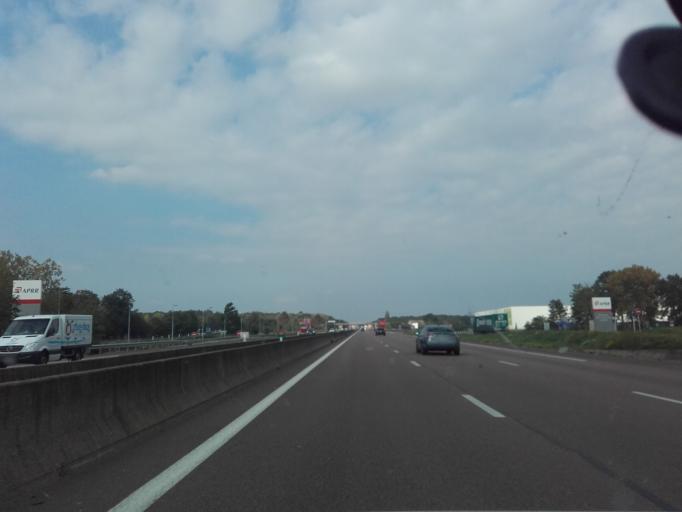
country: FR
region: Bourgogne
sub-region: Departement de Saone-et-Loire
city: Varennes-le-Grand
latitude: 46.6939
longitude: 4.8436
